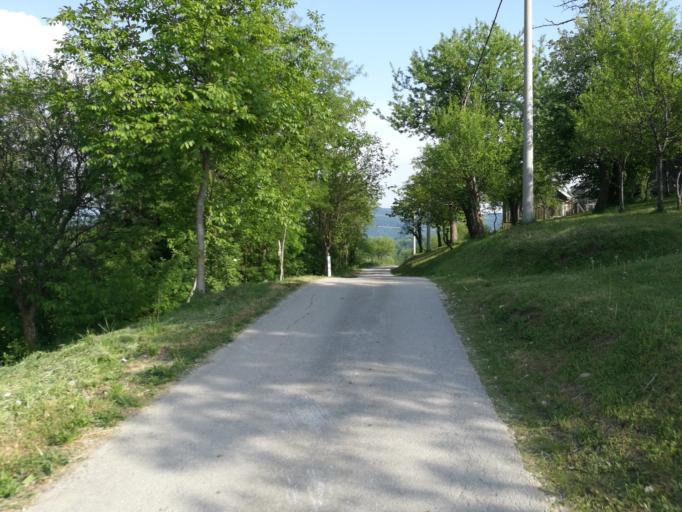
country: HR
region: Krapinsko-Zagorska
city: Radoboj
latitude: 46.2350
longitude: 15.9084
